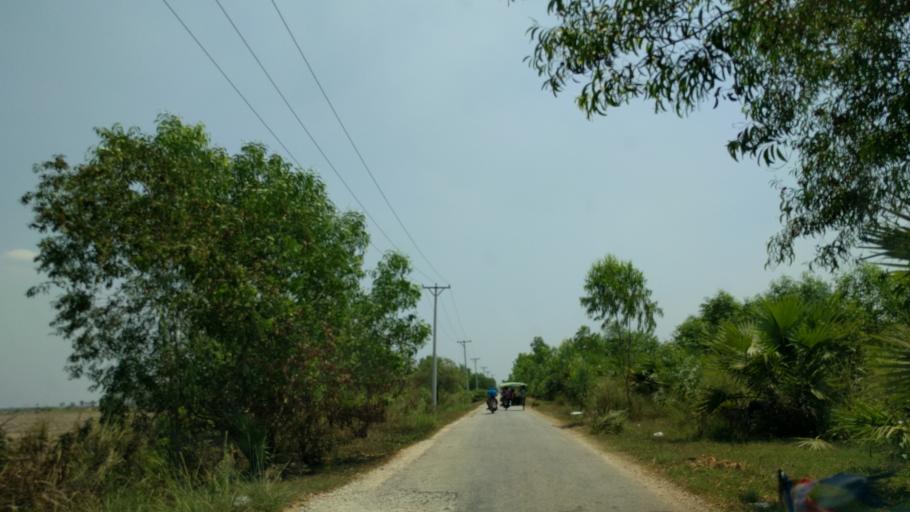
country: MM
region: Mon
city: Martaban
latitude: 16.5858
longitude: 97.6680
